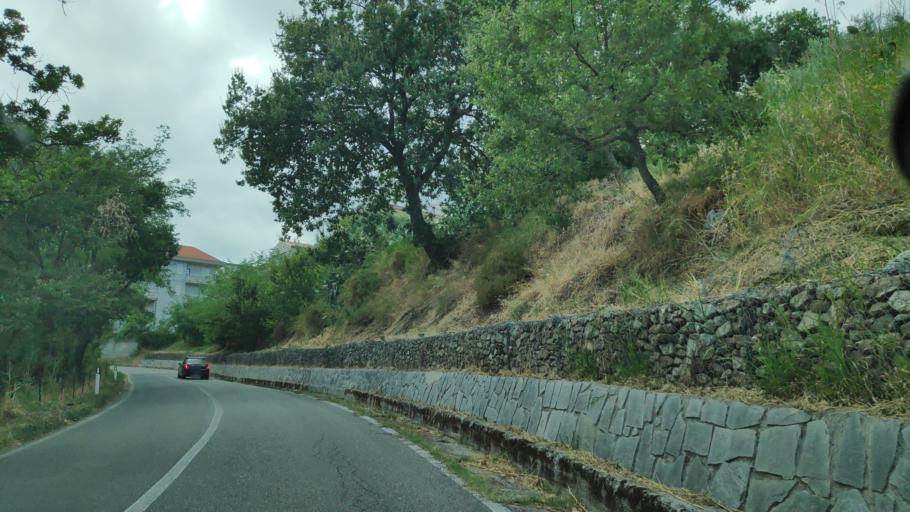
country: IT
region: Calabria
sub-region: Provincia di Catanzaro
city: Santa Caterina dello Ionio
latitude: 38.5314
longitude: 16.5240
